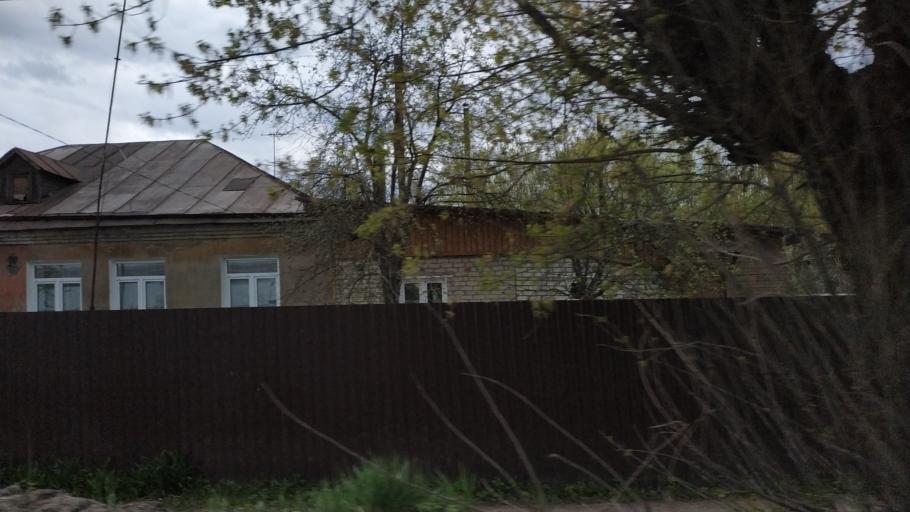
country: RU
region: Moskovskaya
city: Pavlovskiy Posad
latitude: 55.7722
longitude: 38.6890
